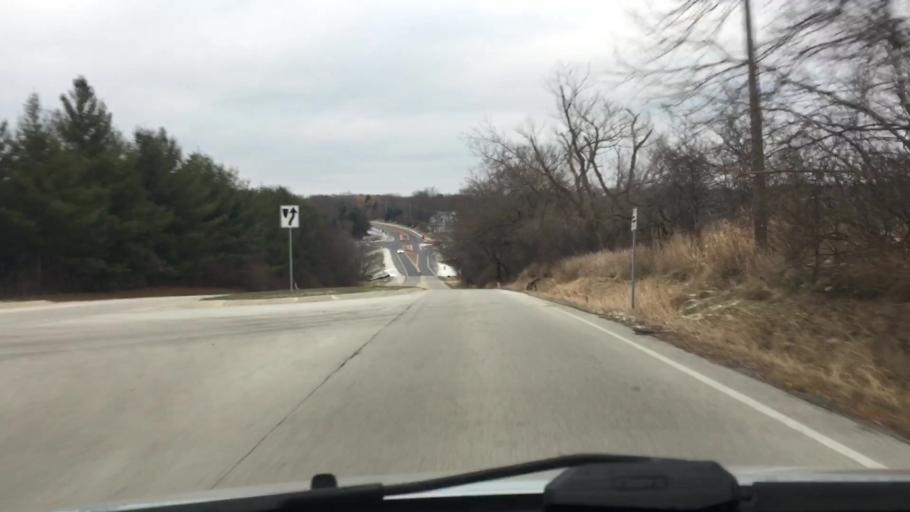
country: US
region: Wisconsin
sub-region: Waukesha County
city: Pewaukee
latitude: 43.1026
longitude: -88.2696
